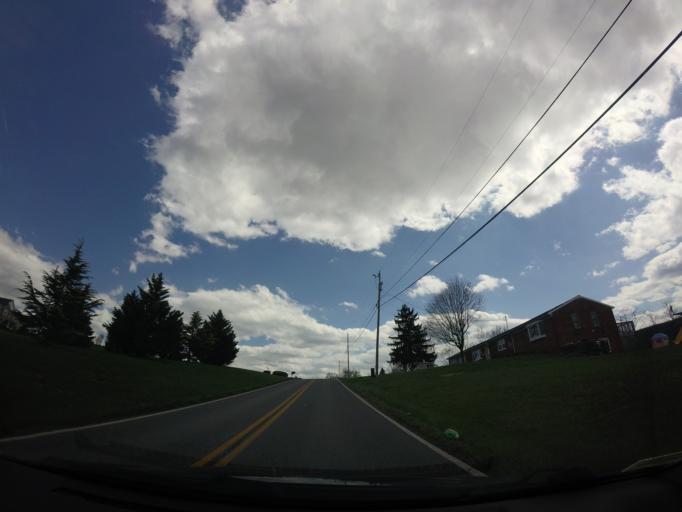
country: US
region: Maryland
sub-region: Washington County
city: Keedysville
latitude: 39.4283
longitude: -77.6747
